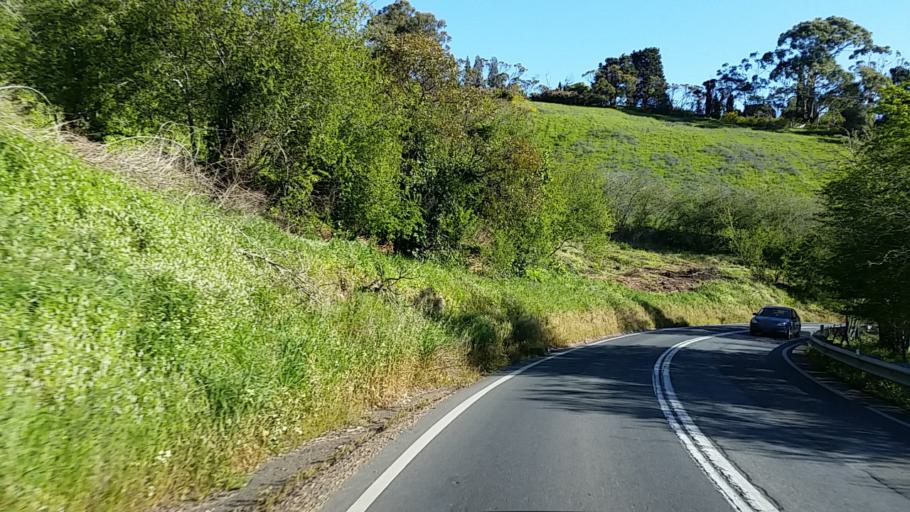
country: AU
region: South Australia
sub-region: Adelaide Hills
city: Adelaide Hills
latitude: -34.9244
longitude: 138.7237
